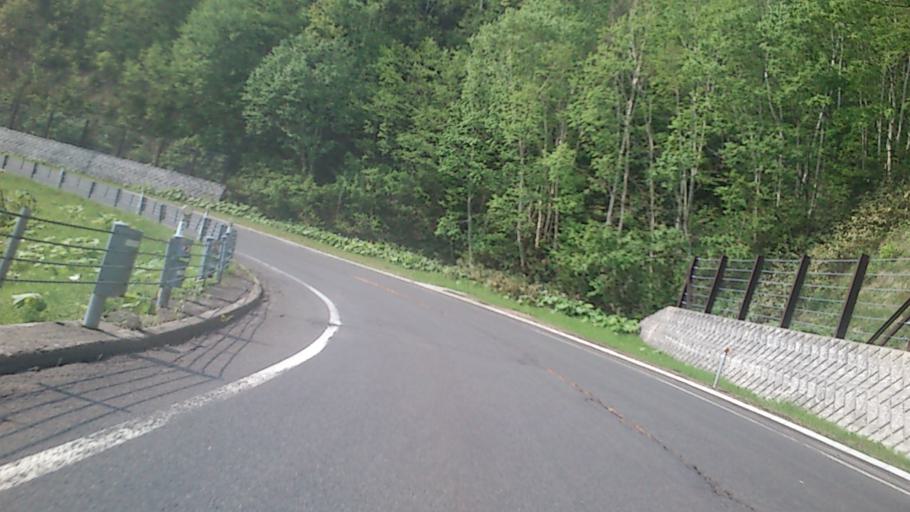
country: JP
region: Hokkaido
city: Bihoro
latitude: 43.4616
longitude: 144.2423
